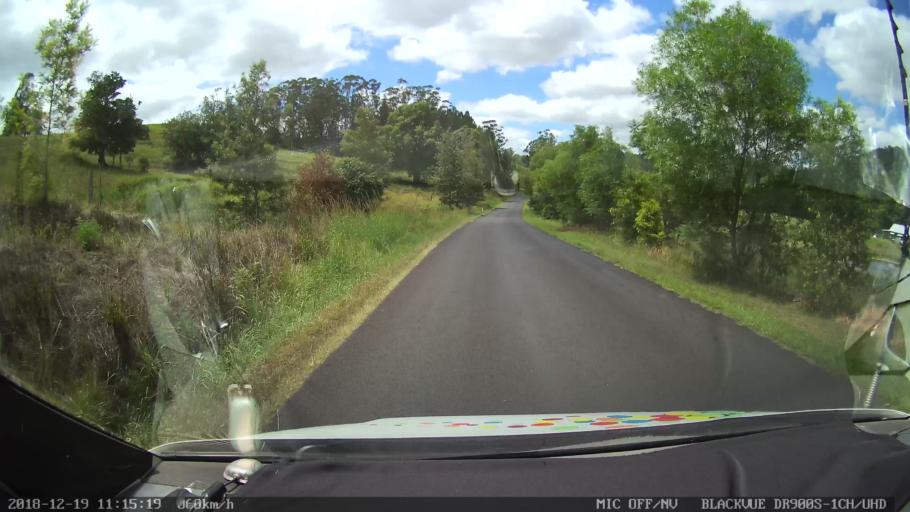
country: AU
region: New South Wales
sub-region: Lismore Municipality
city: Nimbin
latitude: -28.6669
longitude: 153.2774
